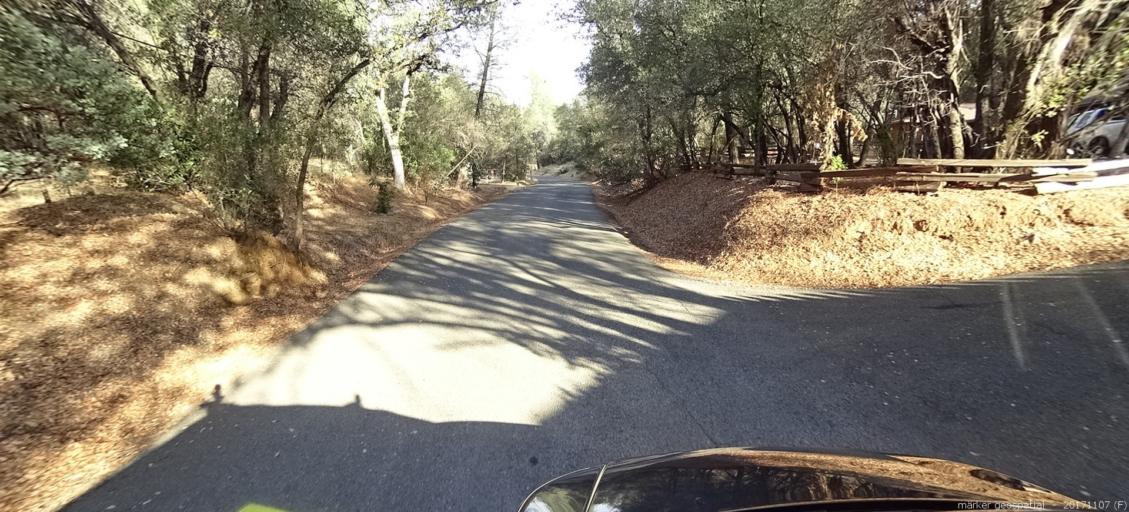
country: US
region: California
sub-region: Shasta County
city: Shasta
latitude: 40.5368
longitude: -122.4557
